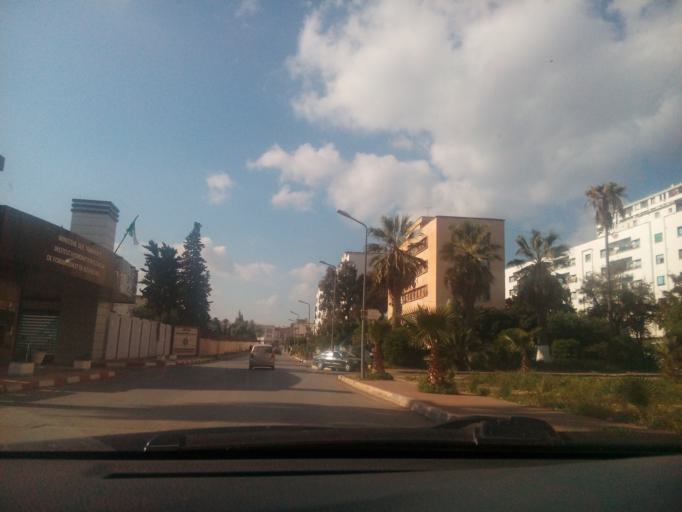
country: DZ
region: Oran
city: Oran
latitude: 35.7031
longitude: -0.6045
